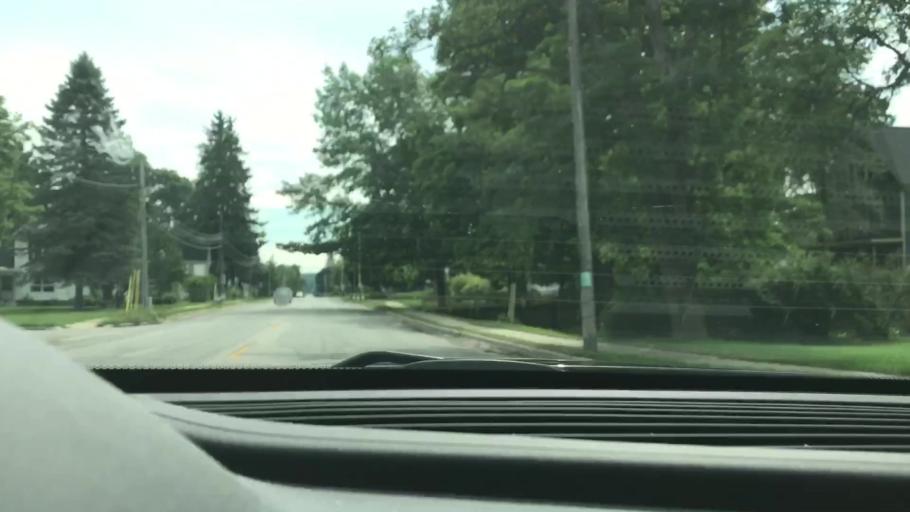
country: US
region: Michigan
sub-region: Antrim County
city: Bellaire
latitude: 45.0689
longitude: -85.2642
